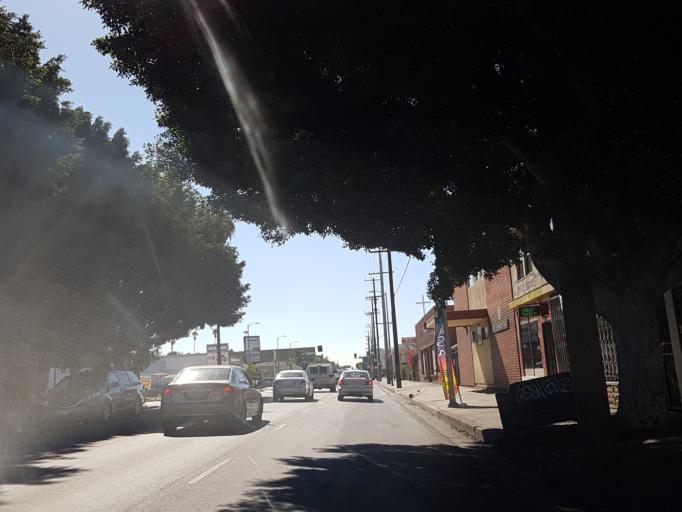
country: US
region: California
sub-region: Los Angeles County
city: Hollywood
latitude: 34.0415
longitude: -118.3091
